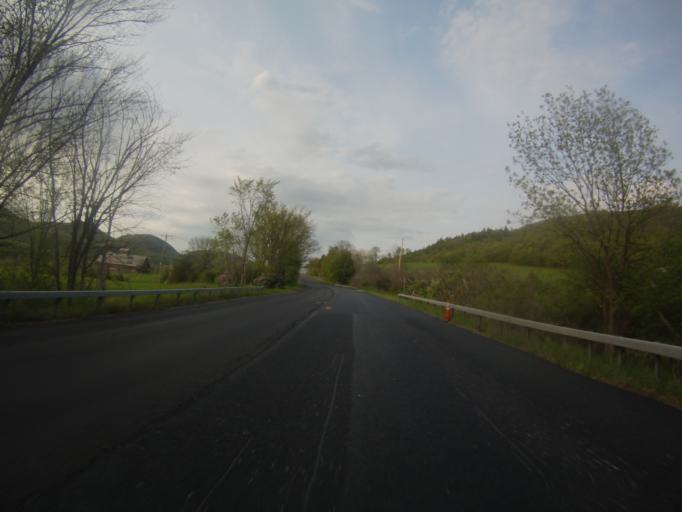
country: US
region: New York
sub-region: Essex County
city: Ticonderoga
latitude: 43.8230
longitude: -73.4710
